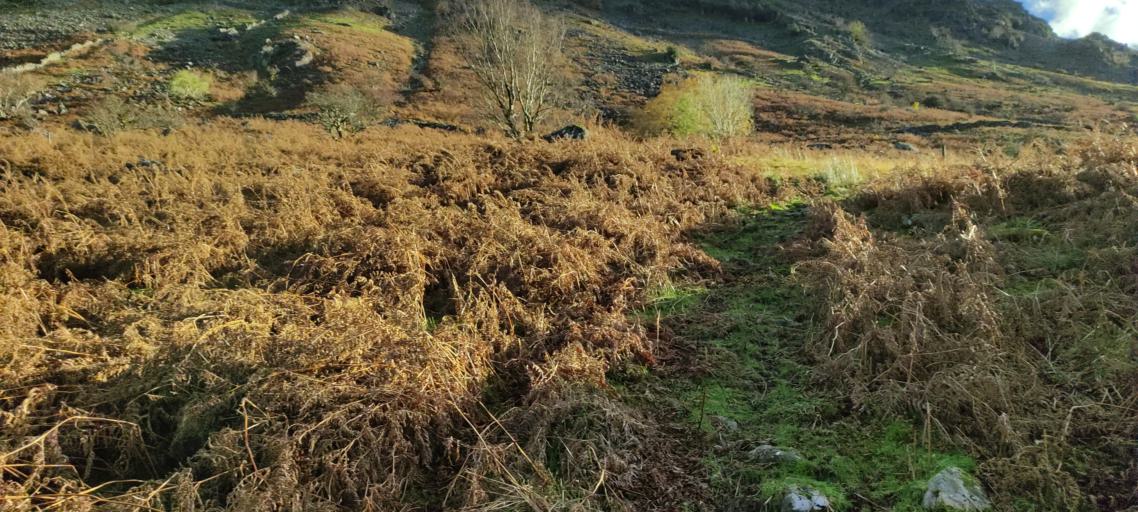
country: GB
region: England
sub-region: Cumbria
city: Keswick
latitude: 54.5102
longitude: -3.1546
